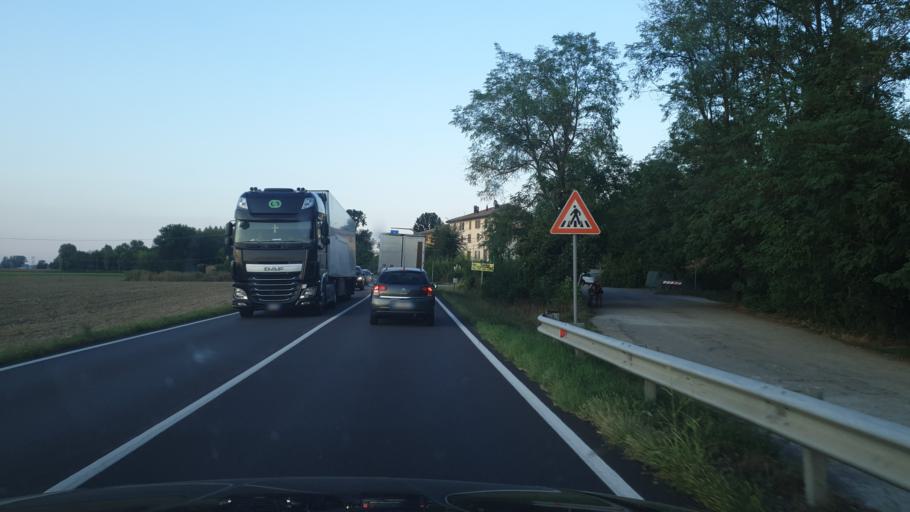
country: IT
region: Emilia-Romagna
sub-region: Provincia di Bologna
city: Progresso
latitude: 44.5592
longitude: 11.3932
